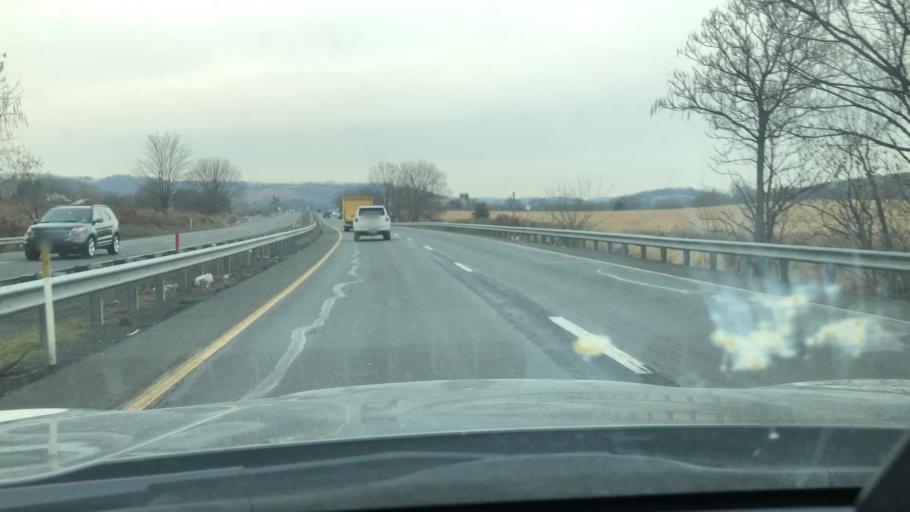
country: US
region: Pennsylvania
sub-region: Berks County
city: New Berlinville
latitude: 40.3425
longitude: -75.6225
